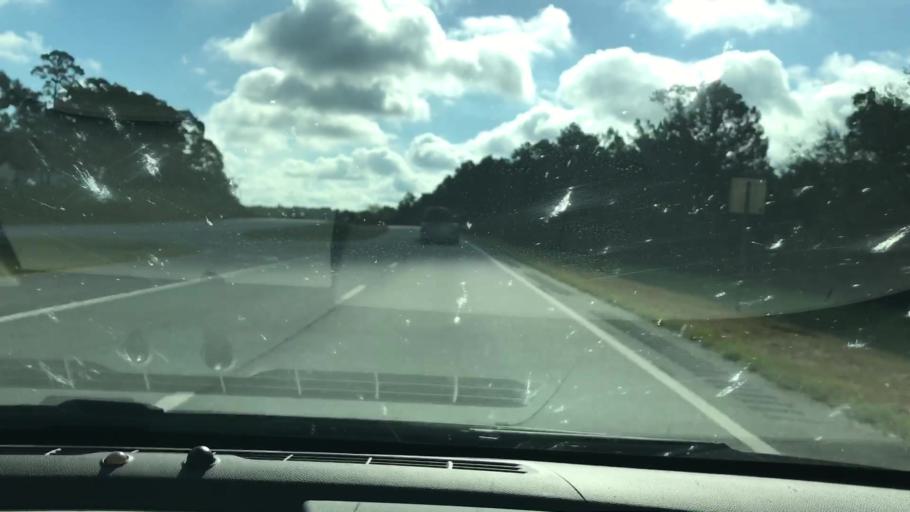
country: US
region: Georgia
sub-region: Worth County
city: Sylvester
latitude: 31.5503
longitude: -83.9678
